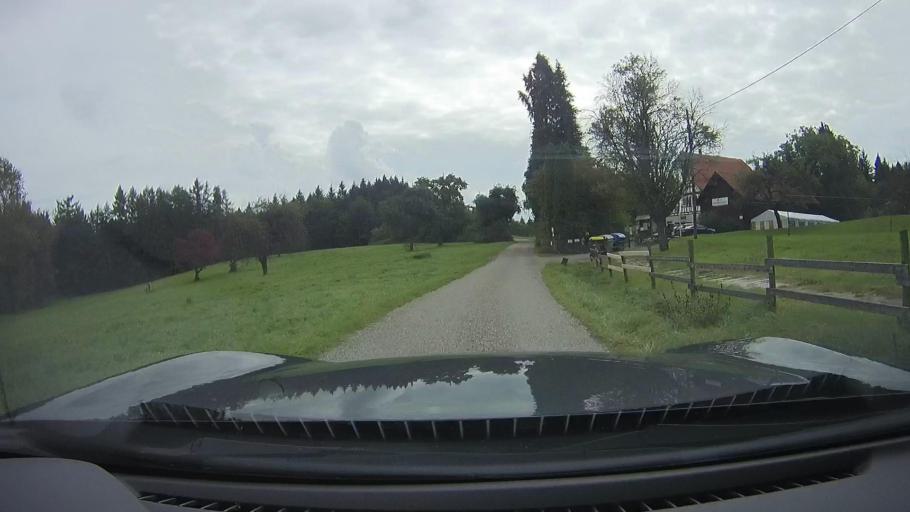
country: DE
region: Baden-Wuerttemberg
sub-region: Regierungsbezirk Stuttgart
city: Sulzbach an der Murr
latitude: 48.9780
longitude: 9.5105
